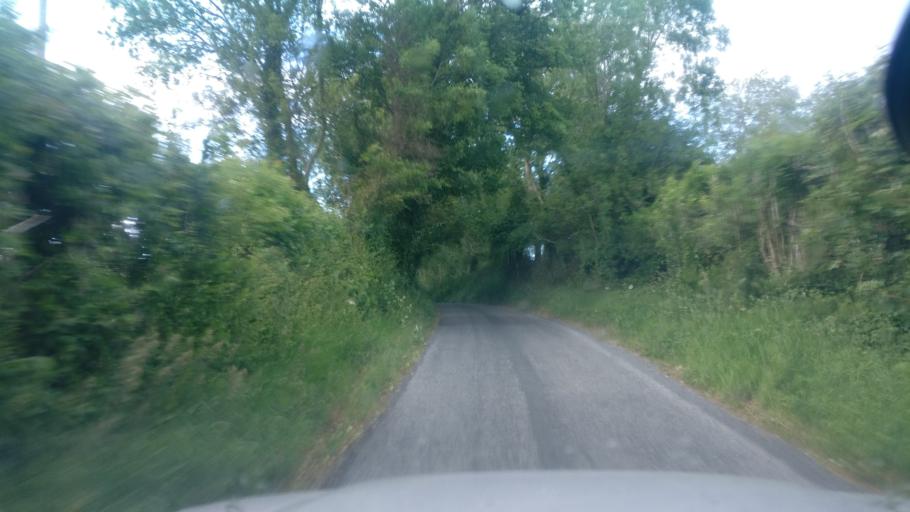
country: IE
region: Connaught
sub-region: County Galway
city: Ballinasloe
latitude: 53.2357
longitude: -8.2305
